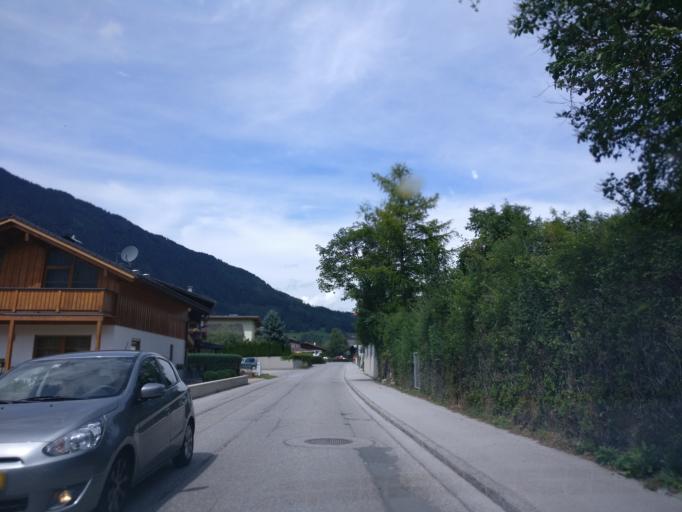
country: AT
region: Tyrol
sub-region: Politischer Bezirk Innsbruck Land
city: Mieders
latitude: 47.1655
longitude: 11.3795
